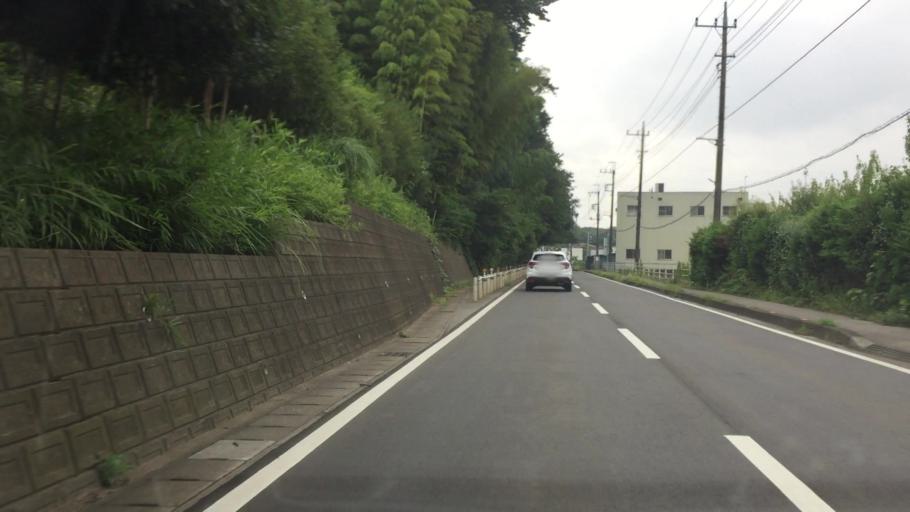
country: JP
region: Chiba
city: Kashiwa
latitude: 35.8138
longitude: 139.9788
